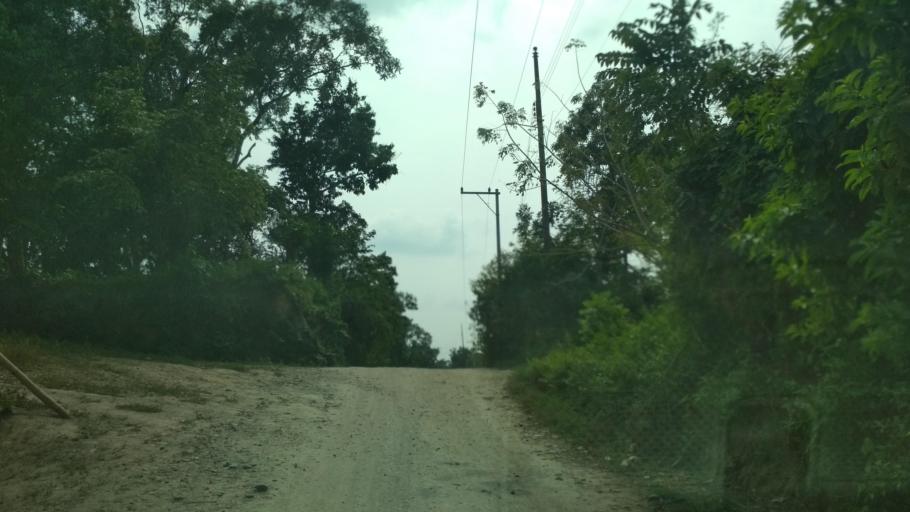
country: MM
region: Kayah
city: Loikaw
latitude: 20.2156
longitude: 97.2848
